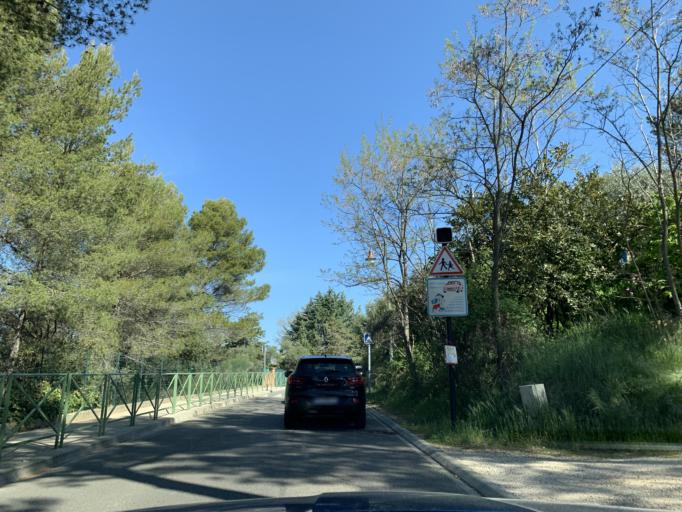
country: FR
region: Provence-Alpes-Cote d'Azur
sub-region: Departement du Vaucluse
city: Roussillon
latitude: 43.8982
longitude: 5.2938
